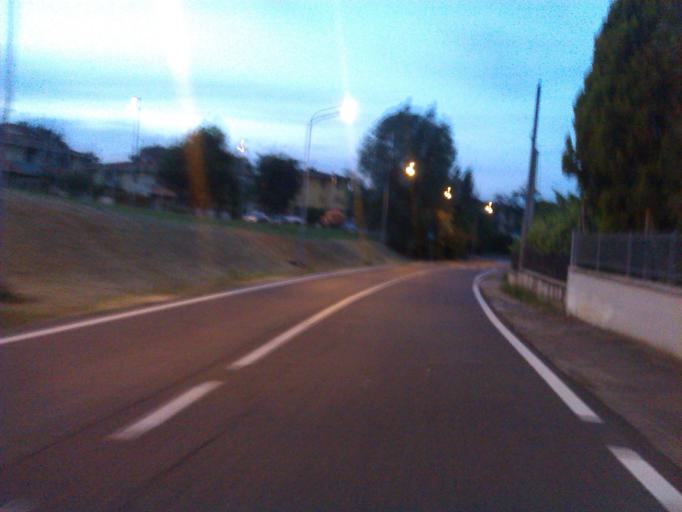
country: IT
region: Tuscany
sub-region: Province of Arezzo
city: Battifolle-Ruscello-Poggiola
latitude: 43.4438
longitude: 11.7869
